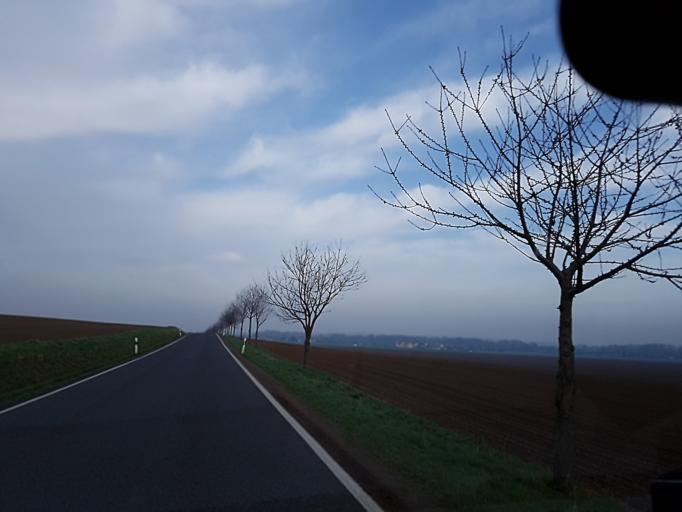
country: DE
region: Saxony
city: Naundorf
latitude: 51.2374
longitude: 13.0993
